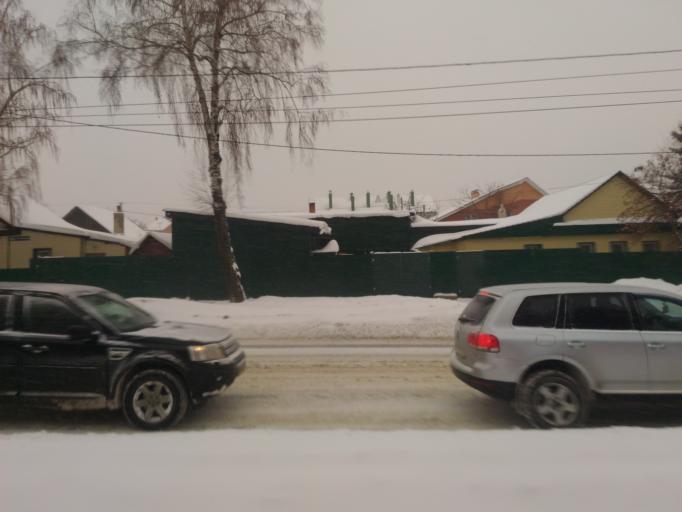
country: RU
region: Ulyanovsk
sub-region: Ulyanovskiy Rayon
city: Ulyanovsk
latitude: 54.3518
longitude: 48.3808
